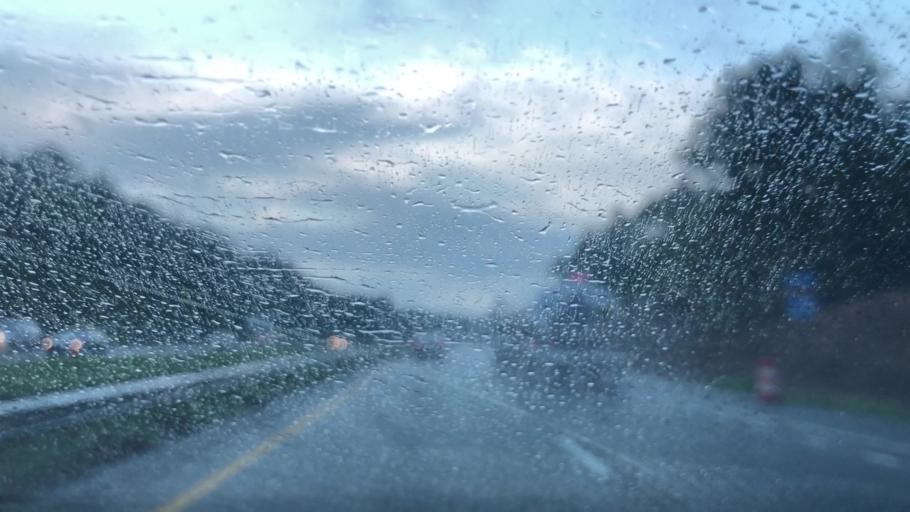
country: US
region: Alabama
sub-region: Shelby County
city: Calera
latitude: 33.1377
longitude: -86.7457
